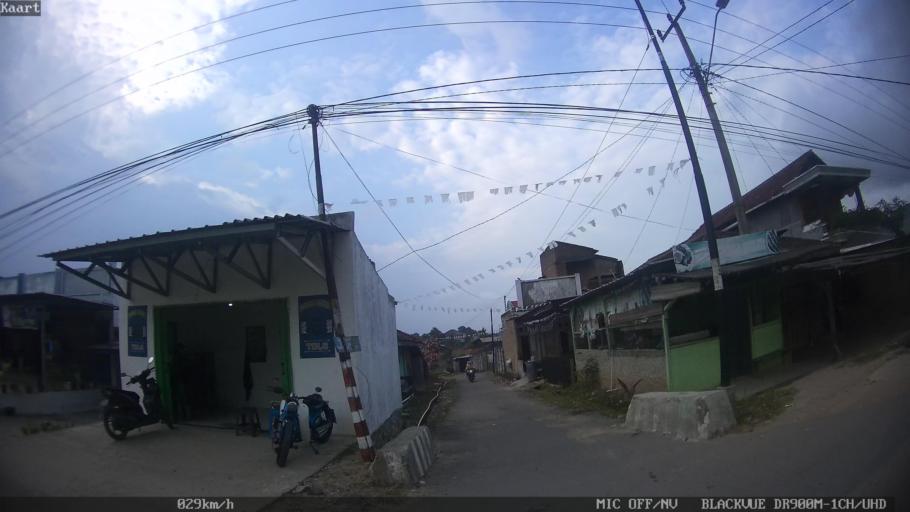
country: ID
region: Lampung
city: Bandarlampung
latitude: -5.4071
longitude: 105.2973
